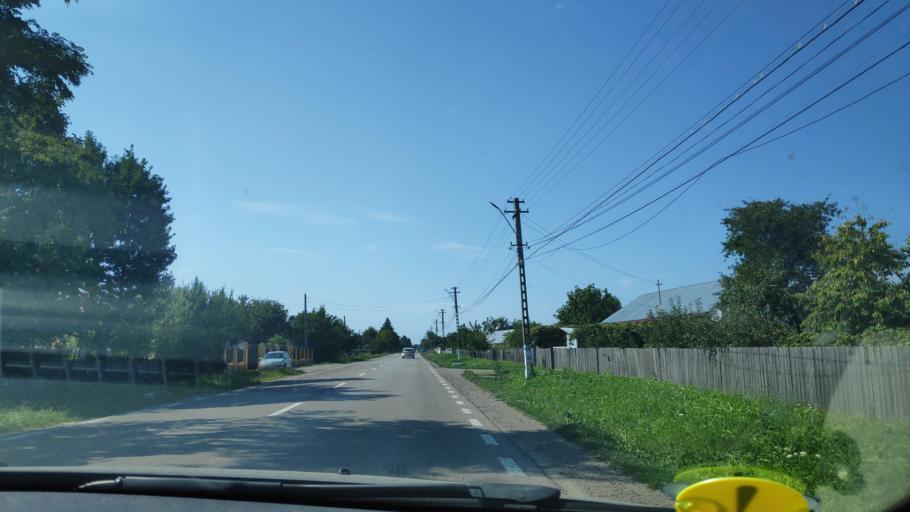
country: RO
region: Suceava
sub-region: Comuna Boroaia
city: Boroaia
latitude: 47.3597
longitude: 26.3423
